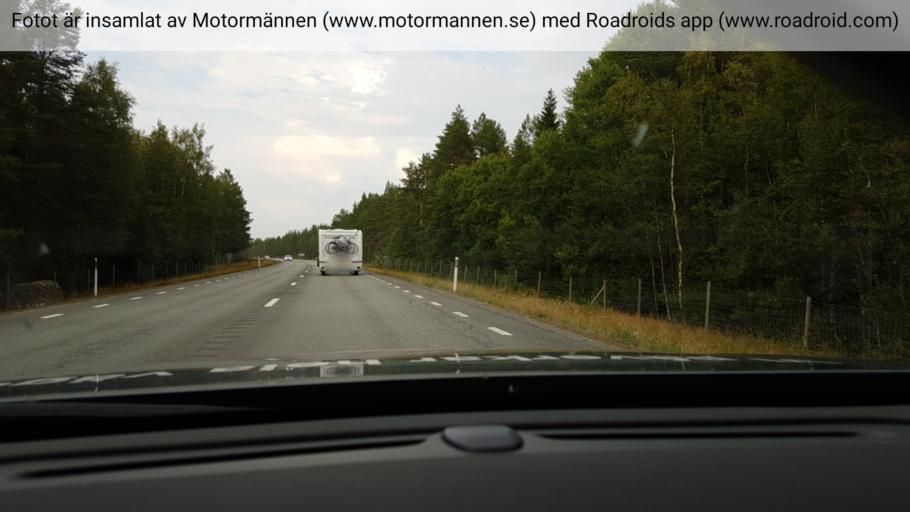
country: SE
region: Vaesterbotten
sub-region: Robertsfors Kommun
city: Robertsfors
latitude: 64.0412
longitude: 20.8466
